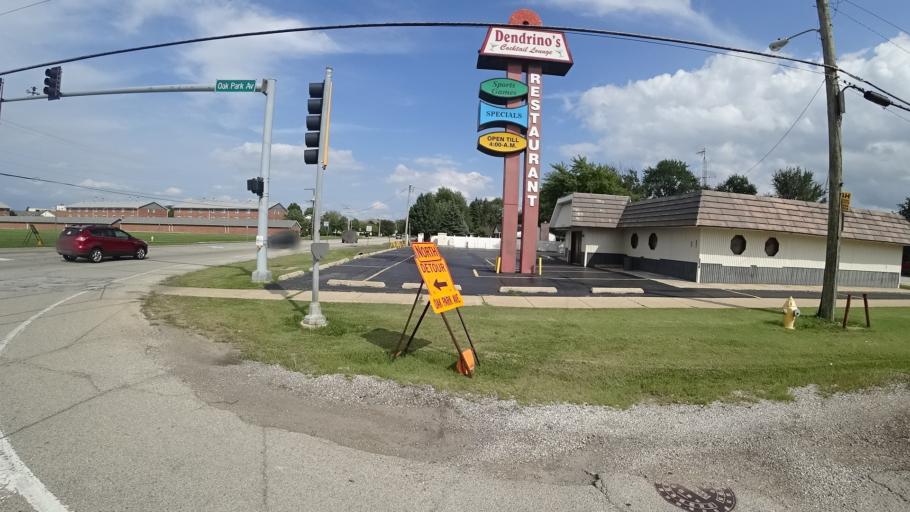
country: US
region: Illinois
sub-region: Cook County
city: Tinley Park
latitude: 41.5585
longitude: -87.7837
